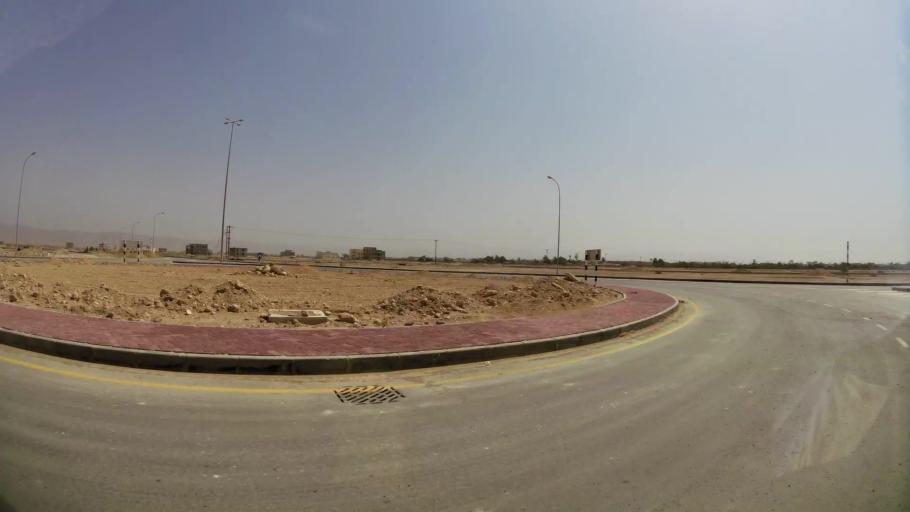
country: OM
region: Zufar
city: Salalah
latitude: 17.0340
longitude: 54.1340
